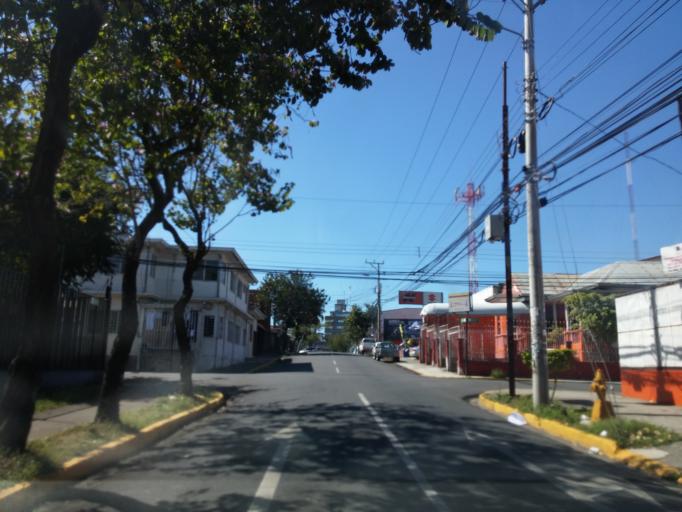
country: CR
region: San Jose
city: San Jose
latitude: 9.9363
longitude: -84.0935
